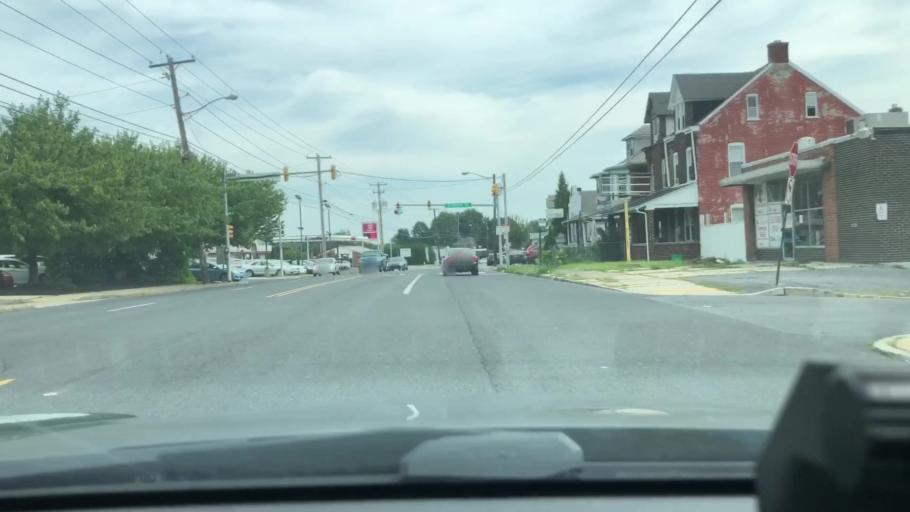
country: US
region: Pennsylvania
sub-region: Lehigh County
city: Fullerton
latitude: 40.6152
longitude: -75.4451
